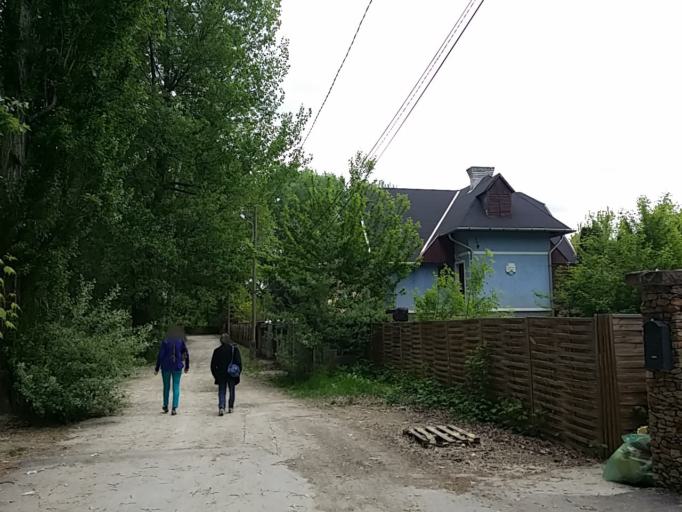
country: HU
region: Pest
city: Szentendre
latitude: 47.6785
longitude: 19.0828
